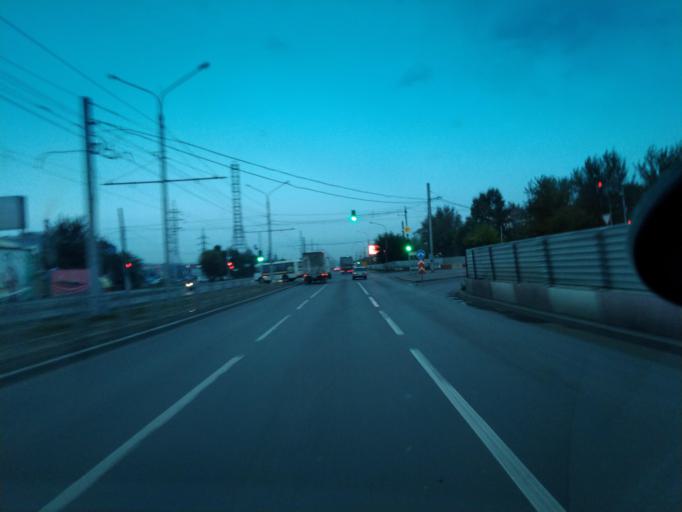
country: RU
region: Krasnoyarskiy
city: Berezovka
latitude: 56.0231
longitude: 93.0154
